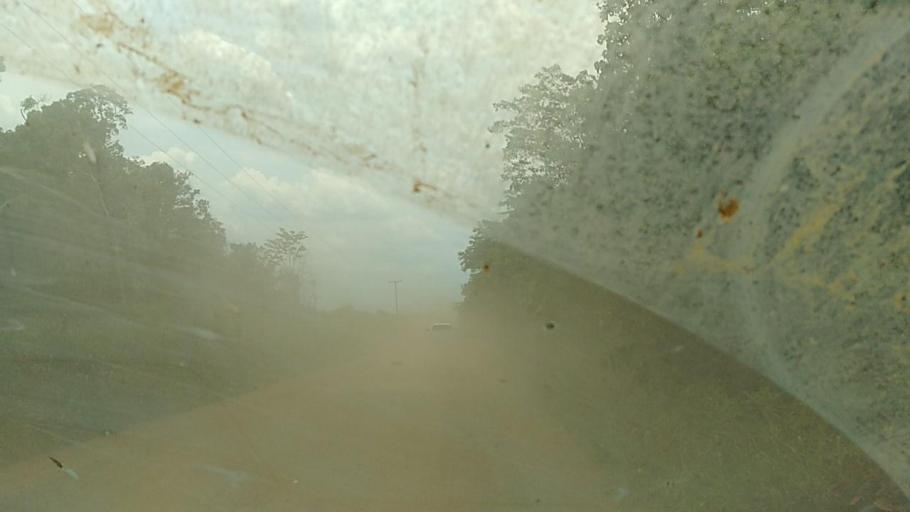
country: BR
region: Rondonia
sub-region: Porto Velho
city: Porto Velho
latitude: -8.9538
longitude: -64.3175
